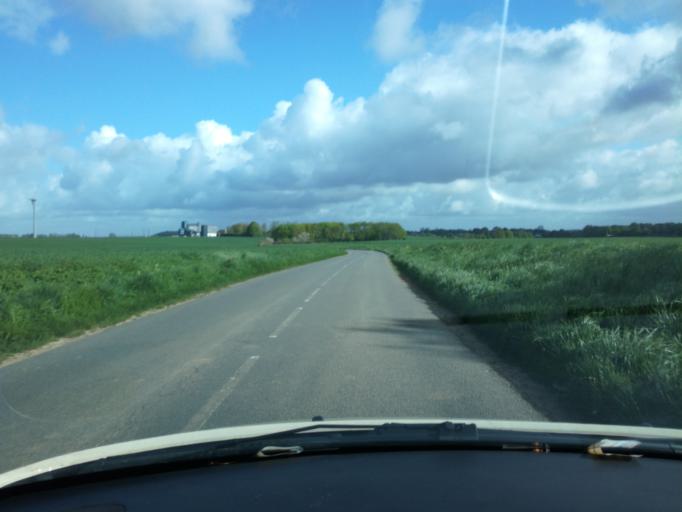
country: FR
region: Picardie
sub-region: Departement de la Somme
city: Beaucamps-le-Vieux
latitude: 49.8920
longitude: 1.8213
